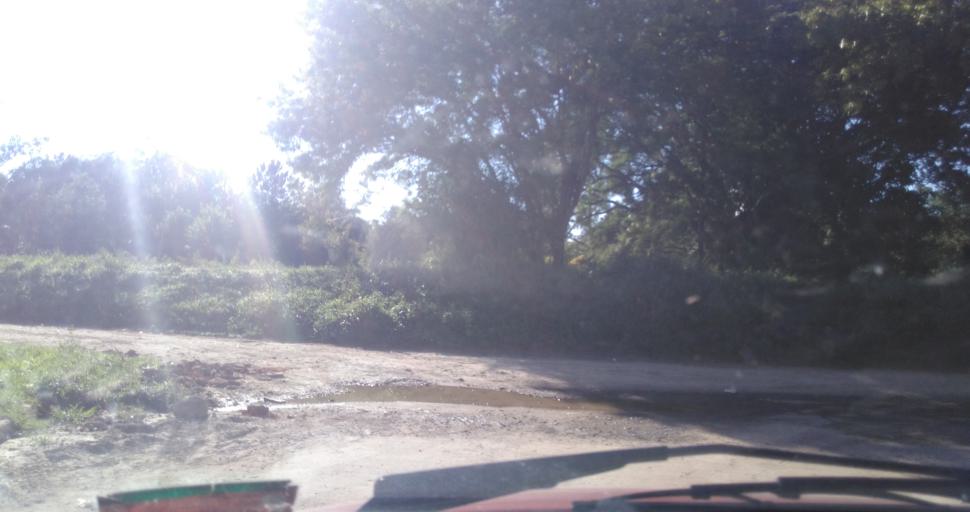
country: AR
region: Chaco
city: Resistencia
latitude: -27.4420
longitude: -58.9623
